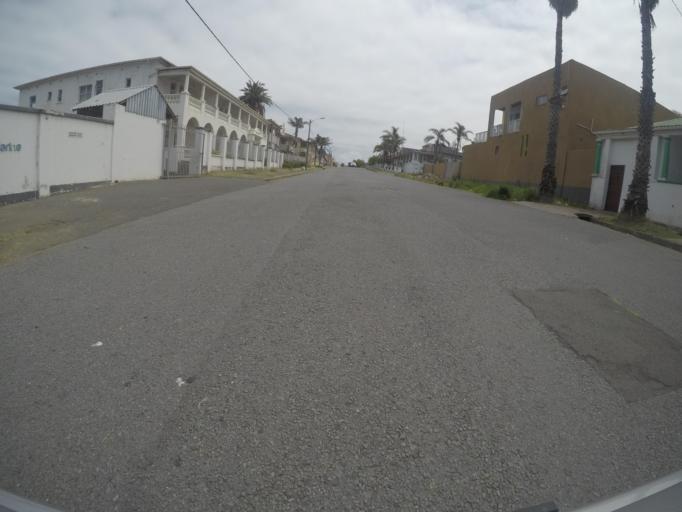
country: ZA
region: Eastern Cape
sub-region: Buffalo City Metropolitan Municipality
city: East London
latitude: -33.0204
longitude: 27.9158
